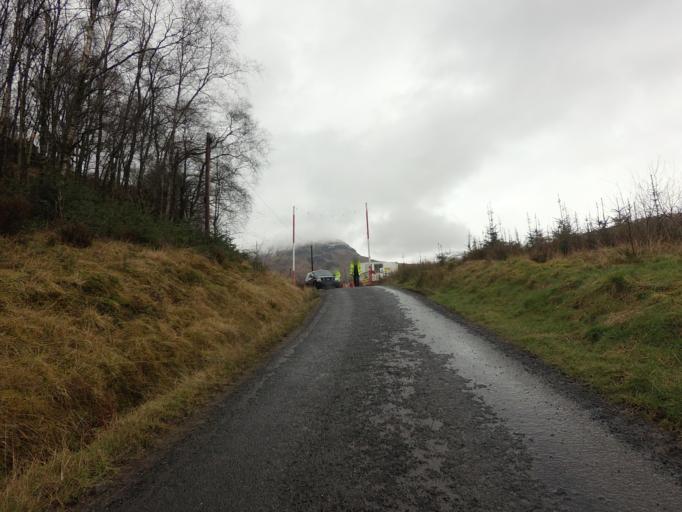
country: GB
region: Scotland
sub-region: West Dunbartonshire
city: Balloch
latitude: 56.2610
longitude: -4.5797
